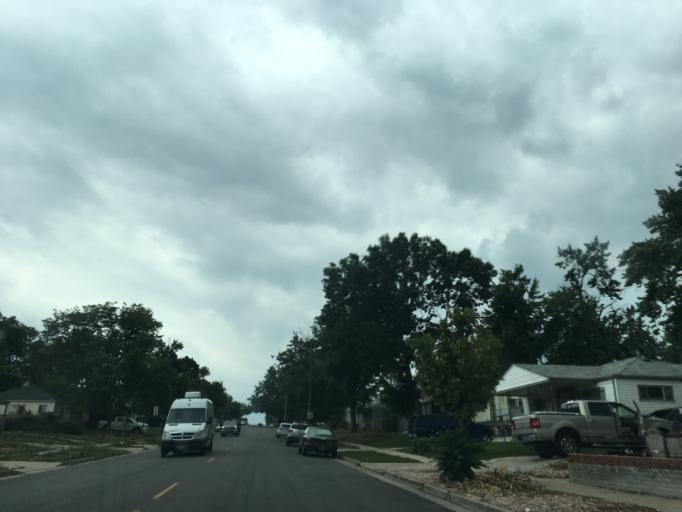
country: US
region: Colorado
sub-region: Arapahoe County
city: Sheridan
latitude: 39.6879
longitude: -105.0158
